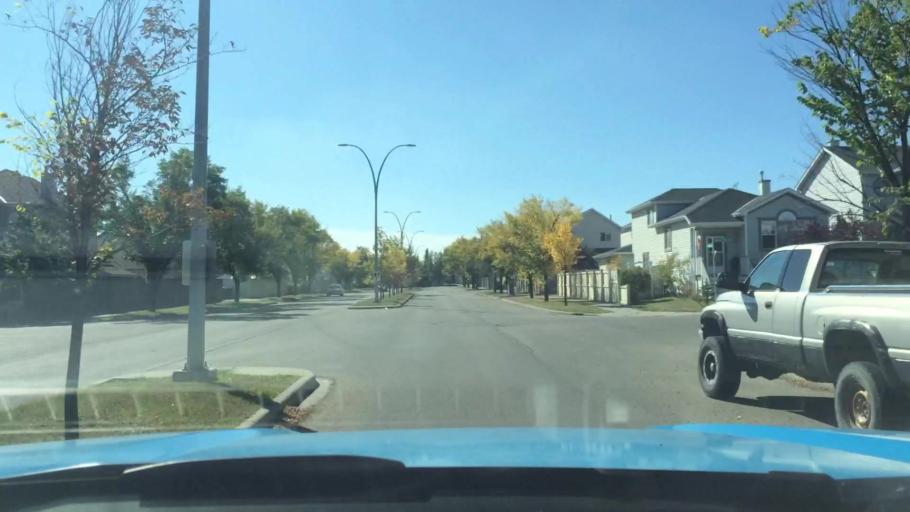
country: CA
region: Alberta
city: Calgary
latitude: 50.9041
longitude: -114.1055
